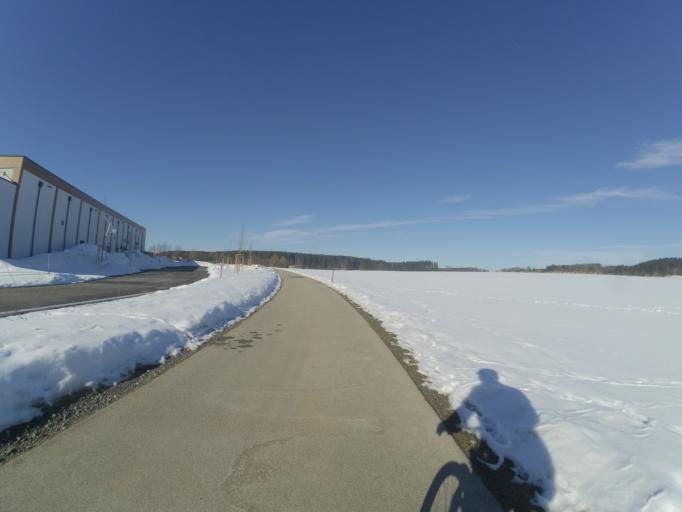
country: DE
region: Bavaria
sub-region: Upper Bavaria
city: Aying
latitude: 47.9477
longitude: 11.7927
